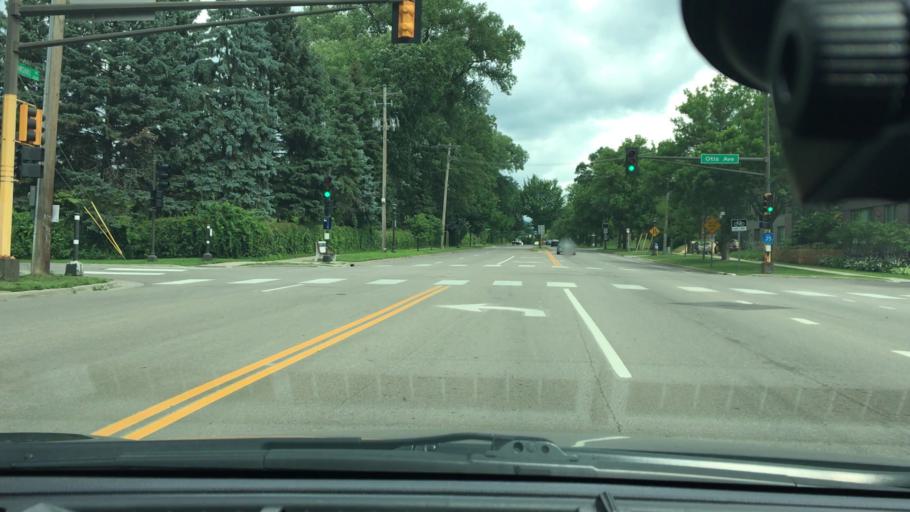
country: US
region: Minnesota
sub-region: Ramsey County
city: Lauderdale
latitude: 44.9481
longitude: -93.1983
